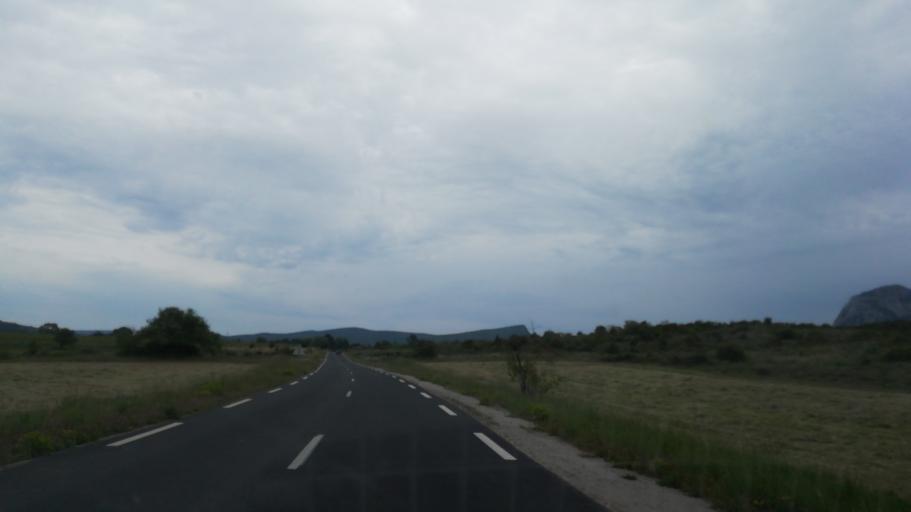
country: FR
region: Languedoc-Roussillon
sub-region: Departement de l'Herault
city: Saint-Martin-de-Londres
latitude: 43.7940
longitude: 3.7704
